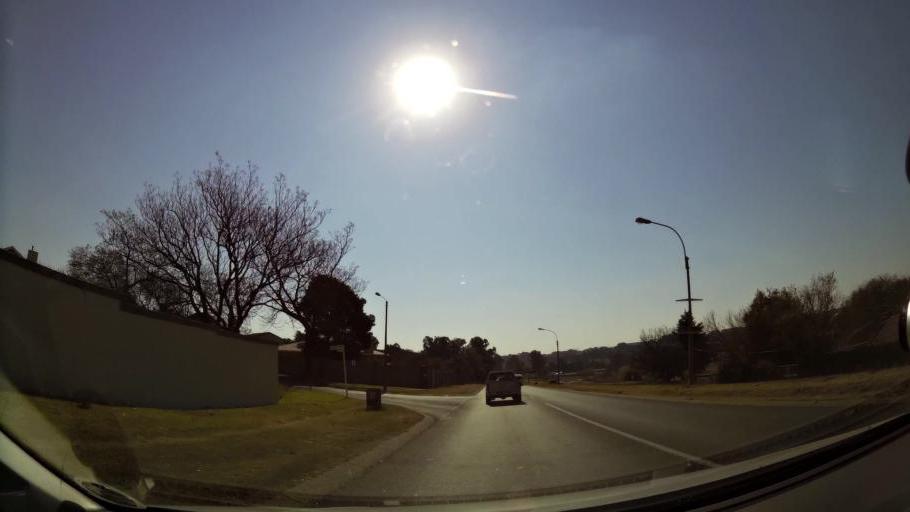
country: ZA
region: Gauteng
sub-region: City of Johannesburg Metropolitan Municipality
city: Modderfontein
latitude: -26.1101
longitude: 28.1684
